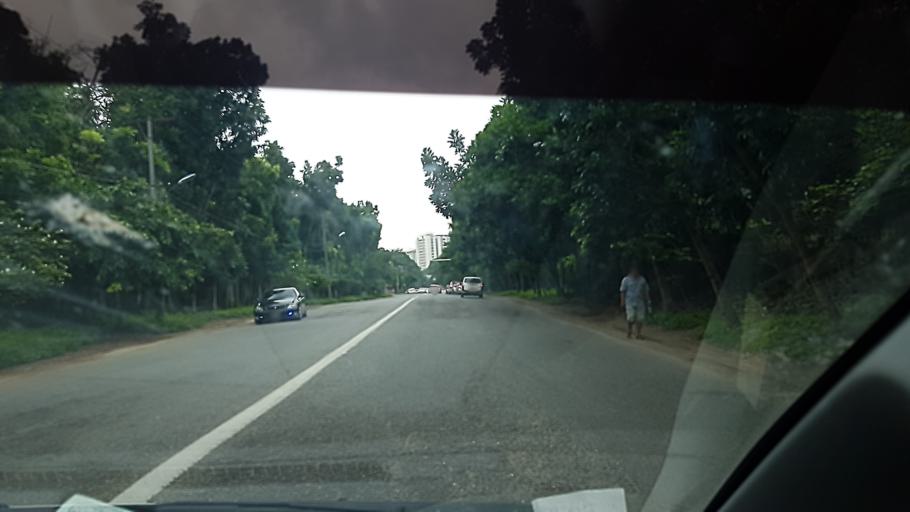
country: MM
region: Yangon
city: Yangon
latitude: 16.7923
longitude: 96.1326
